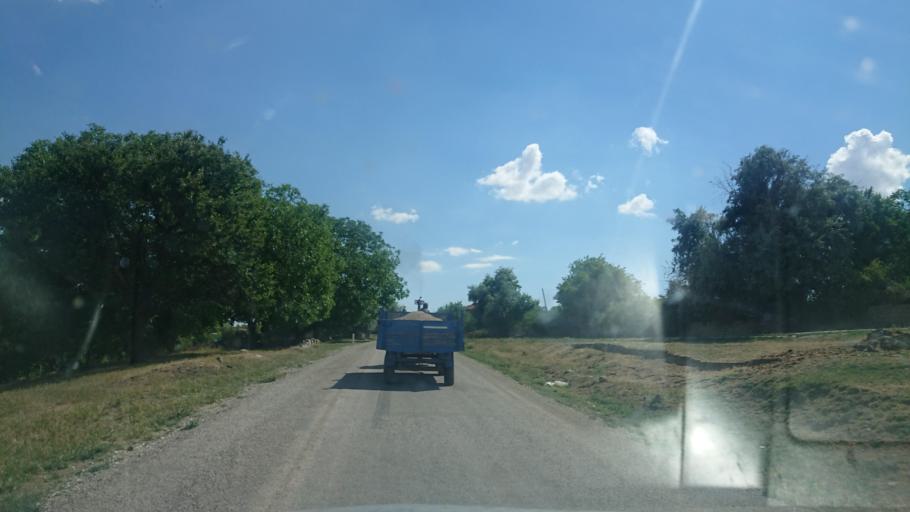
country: TR
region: Aksaray
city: Agacoren
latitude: 38.7747
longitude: 33.7872
